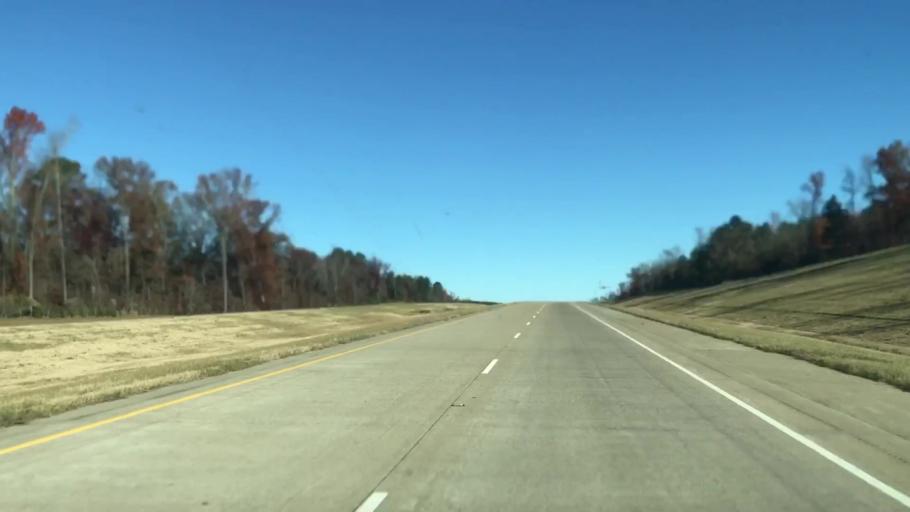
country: US
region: Louisiana
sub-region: Caddo Parish
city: Oil City
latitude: 32.7903
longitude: -93.8877
